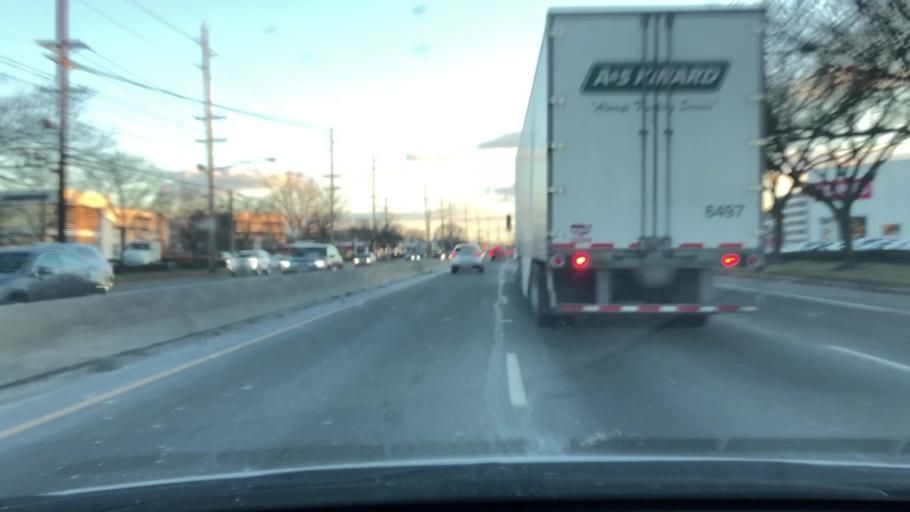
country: US
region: New Jersey
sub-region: Bergen County
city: Paramus
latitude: 40.9564
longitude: -74.0740
